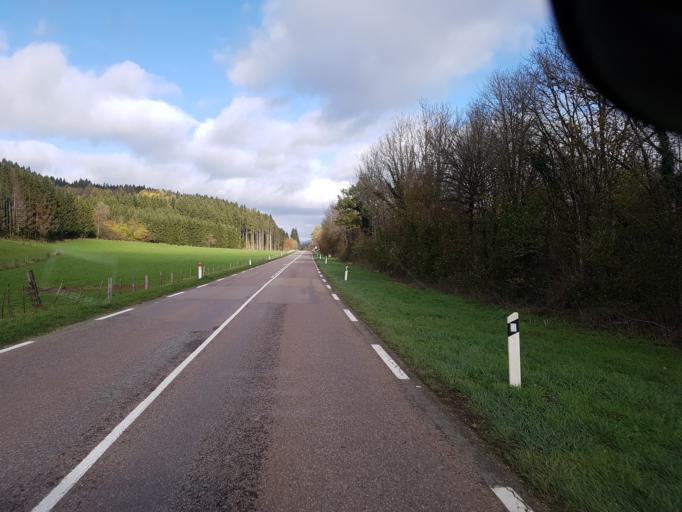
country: FR
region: Franche-Comte
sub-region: Departement du Jura
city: Champagnole
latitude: 46.6984
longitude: 5.9309
